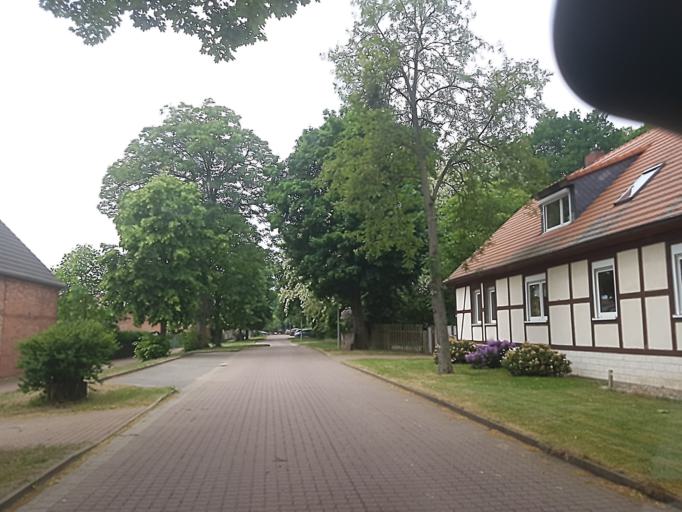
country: DE
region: Saxony-Anhalt
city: Lindau
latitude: 52.0790
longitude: 12.2452
